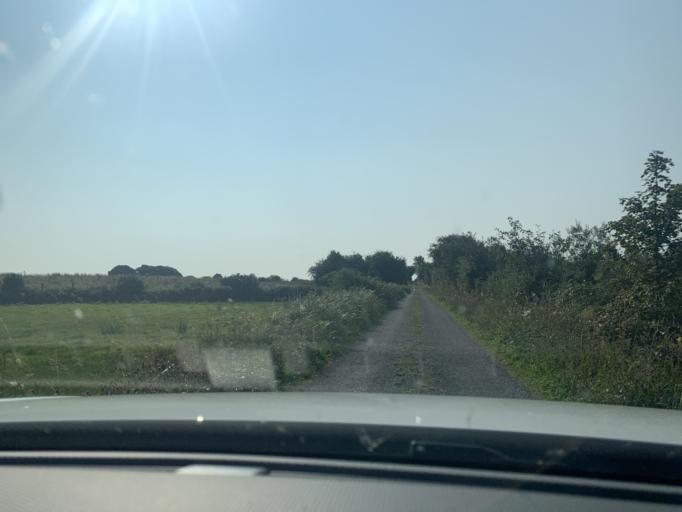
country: IE
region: Connaught
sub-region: Maigh Eo
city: Ballyhaunis
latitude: 53.8099
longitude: -8.7459
